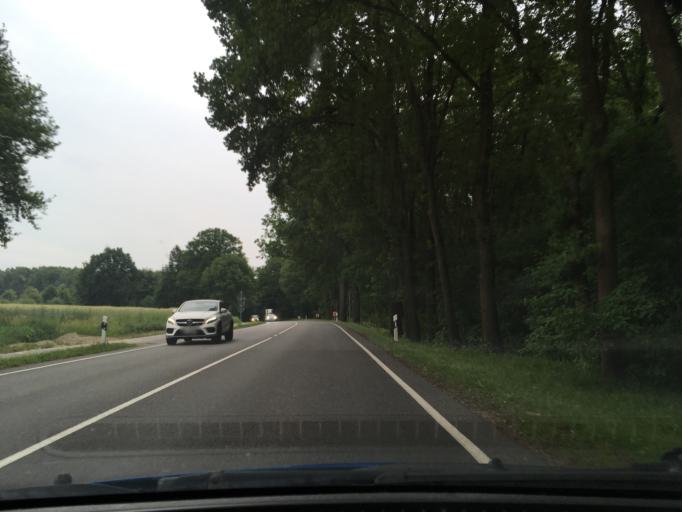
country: DE
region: Lower Saxony
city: Appel
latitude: 53.4021
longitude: 9.7887
